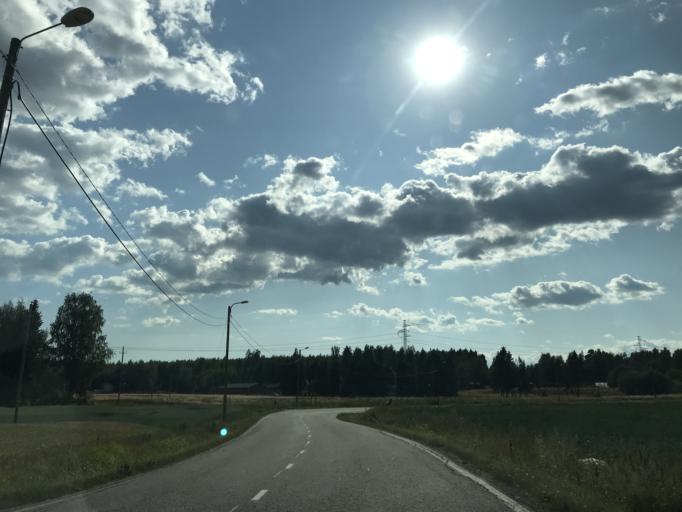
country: FI
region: Uusimaa
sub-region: Helsinki
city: Nurmijaervi
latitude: 60.4507
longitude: 24.5939
